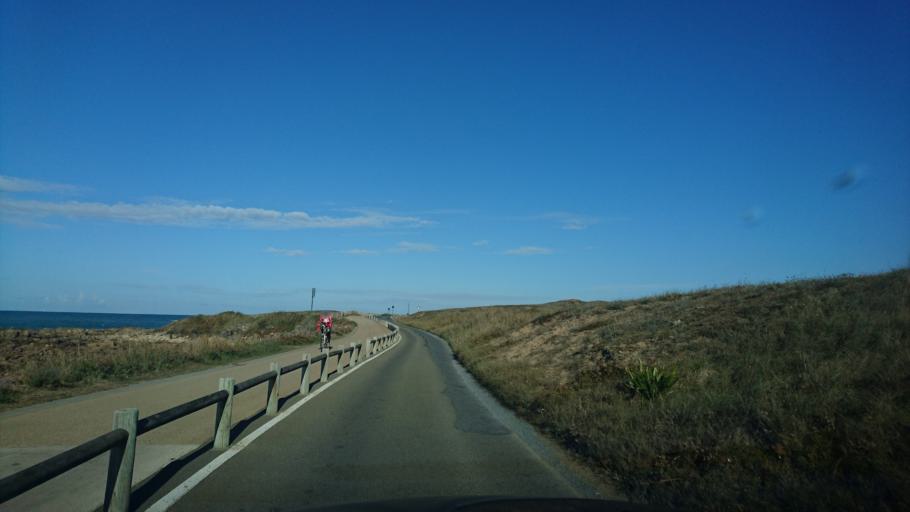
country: FR
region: Pays de la Loire
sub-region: Departement de la Vendee
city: Les Sables-d'Olonne
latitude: 46.5089
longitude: -1.8179
